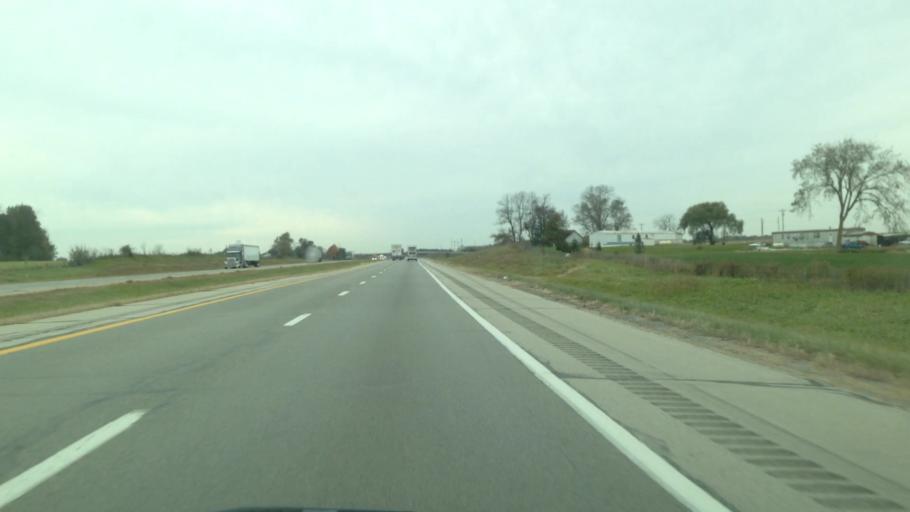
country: US
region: Ohio
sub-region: Williams County
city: Montpelier
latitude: 41.6197
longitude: -84.6821
